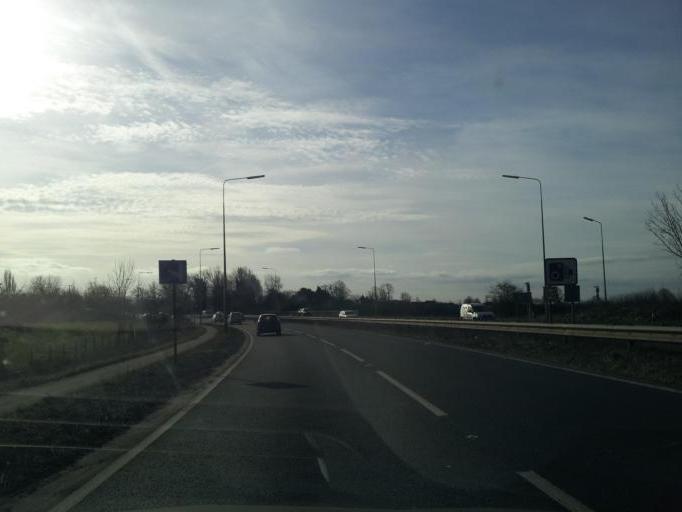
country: GB
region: England
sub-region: Central Bedfordshire
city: Sandy
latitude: 52.1238
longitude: -0.2980
